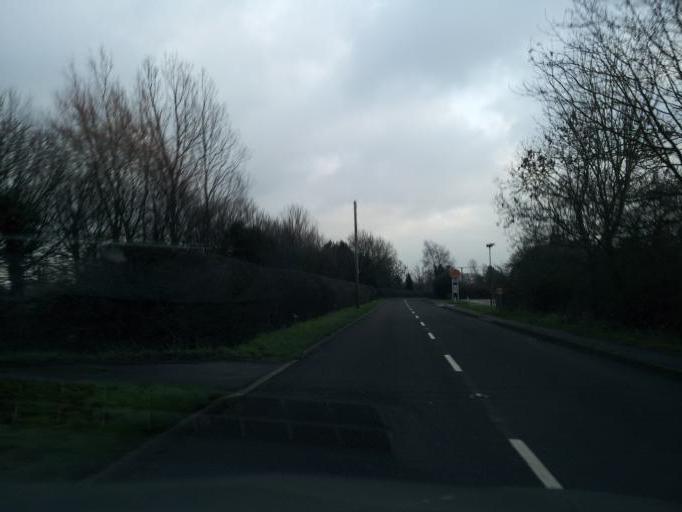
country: GB
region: England
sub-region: Derbyshire
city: Etwall
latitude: 52.8670
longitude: -1.6176
